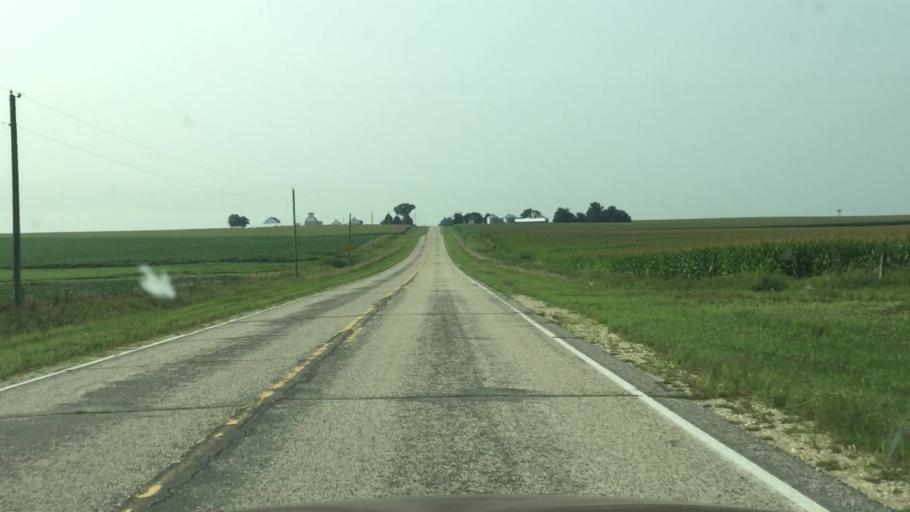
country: US
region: Iowa
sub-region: O'Brien County
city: Sheldon
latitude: 43.2762
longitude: -95.7829
